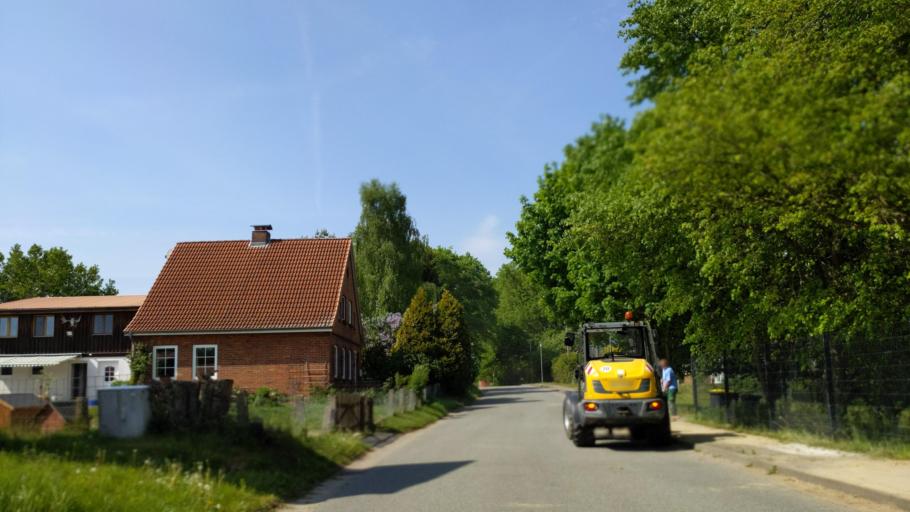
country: DE
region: Mecklenburg-Vorpommern
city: Selmsdorf
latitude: 53.8771
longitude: 10.8186
